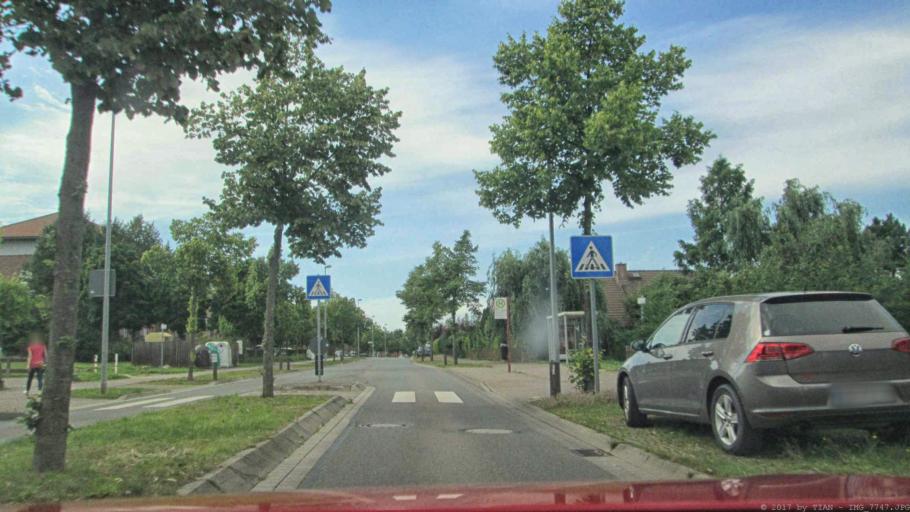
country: DE
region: Lower Saxony
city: Wolfsburg
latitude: 52.4147
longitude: 10.8342
